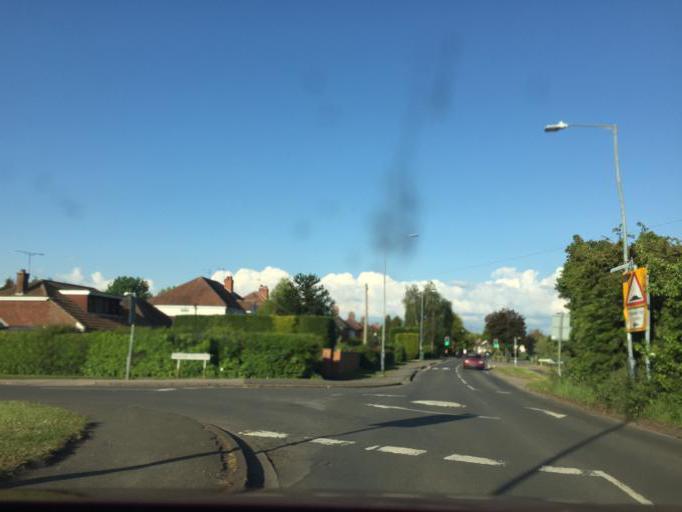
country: GB
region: England
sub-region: Warwickshire
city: Attleborough
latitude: 52.5015
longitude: -1.4435
